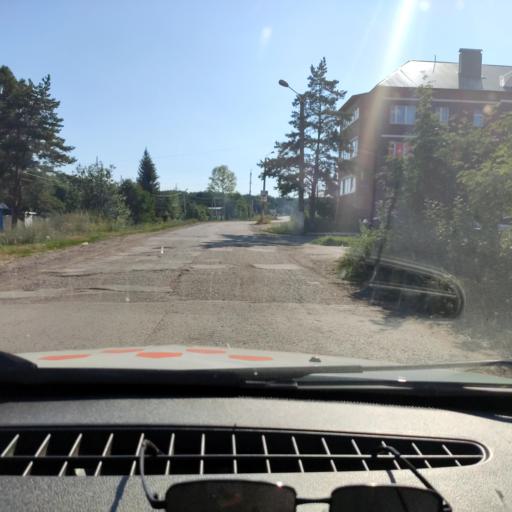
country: RU
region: Bashkortostan
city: Tolbazy
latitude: 54.0055
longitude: 55.8897
